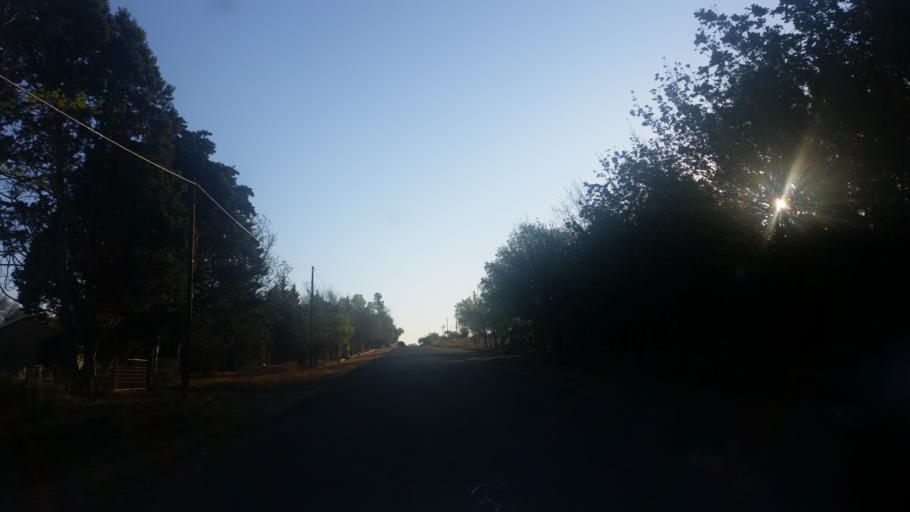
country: ZA
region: Orange Free State
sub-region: Thabo Mofutsanyana District Municipality
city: Phuthaditjhaba
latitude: -28.3160
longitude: 28.6978
